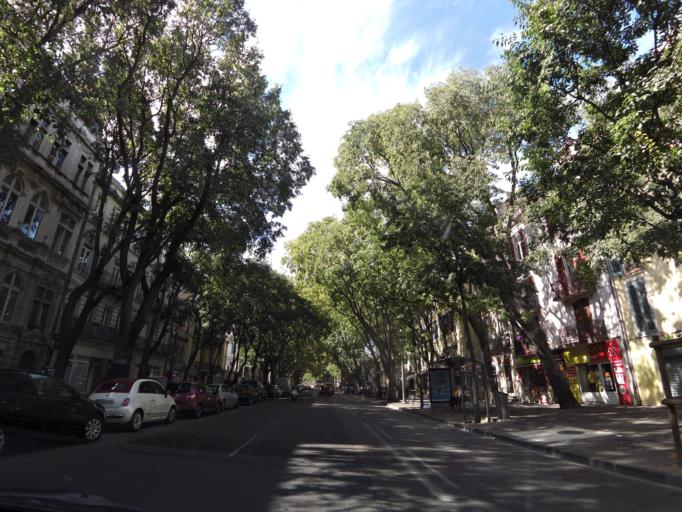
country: FR
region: Languedoc-Roussillon
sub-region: Departement du Gard
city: Nimes
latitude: 43.8405
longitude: 4.3615
